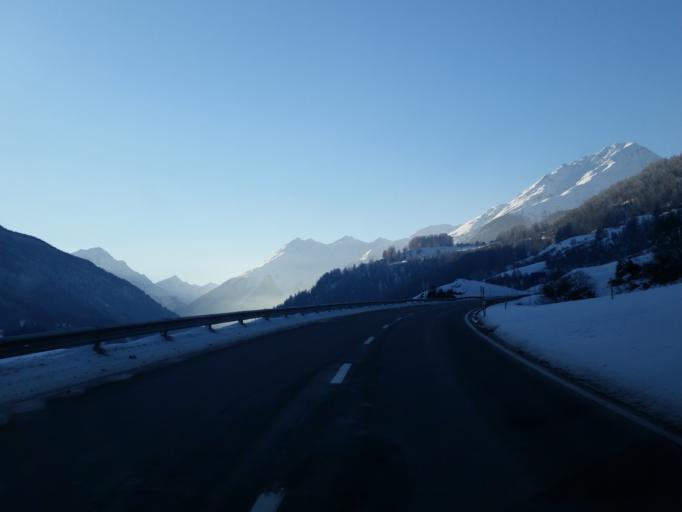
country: CH
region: Grisons
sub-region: Inn District
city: Scuol
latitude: 46.7737
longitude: 10.1940
